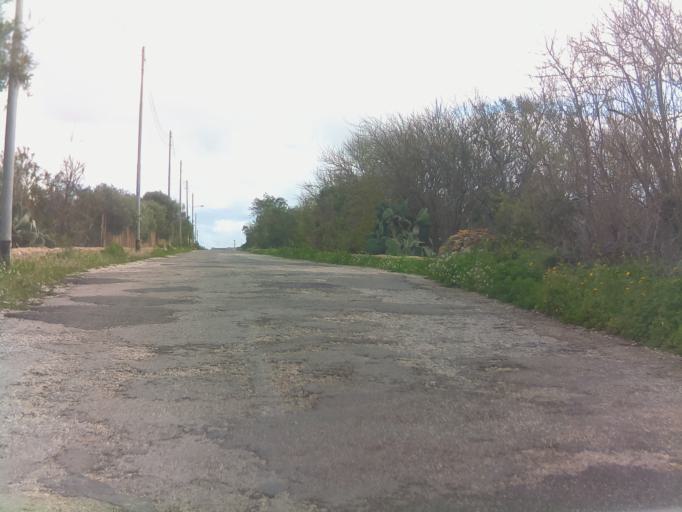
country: MT
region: Il-Mellieha
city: Mellieha
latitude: 35.9882
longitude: 14.3659
